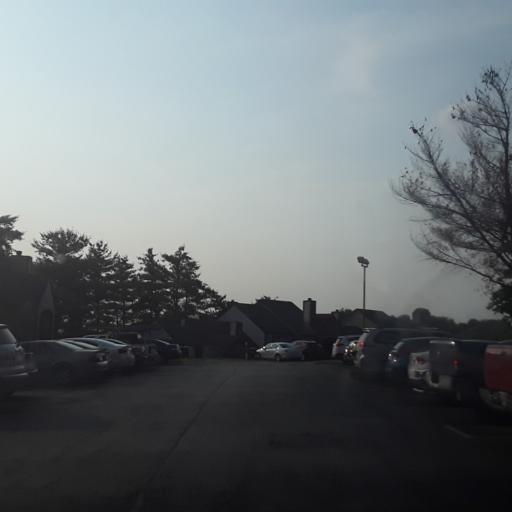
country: US
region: Tennessee
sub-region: Williamson County
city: Brentwood Estates
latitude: 36.0427
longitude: -86.7237
